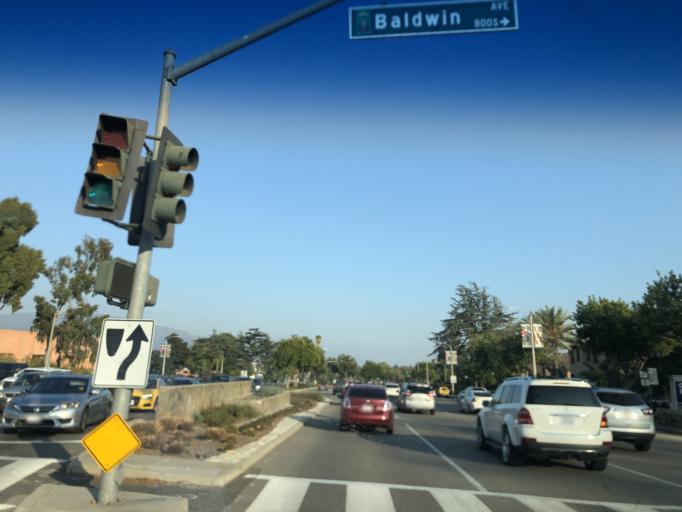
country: US
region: California
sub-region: Los Angeles County
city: Arcadia
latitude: 34.1316
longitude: -118.0546
